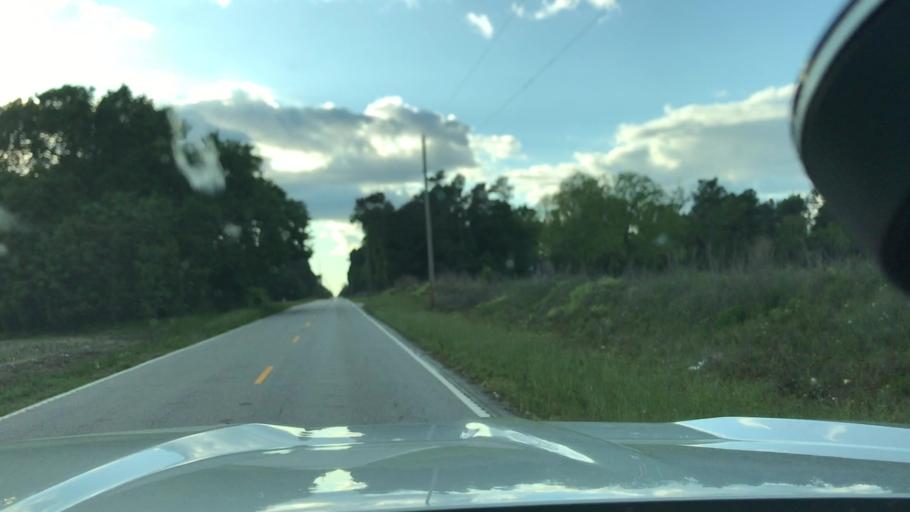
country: US
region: South Carolina
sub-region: Bamberg County
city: Denmark
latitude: 33.4579
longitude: -81.1457
